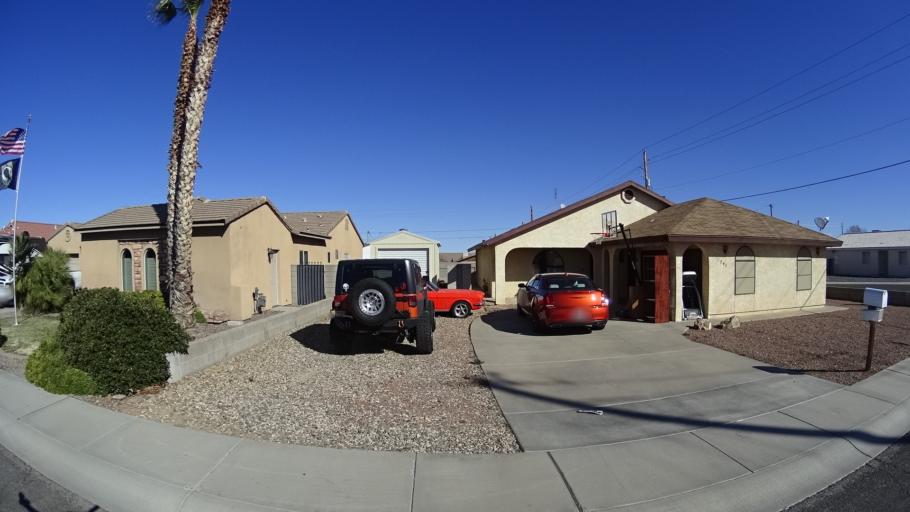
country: US
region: Arizona
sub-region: Mohave County
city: Kingman
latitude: 35.1986
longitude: -114.0139
